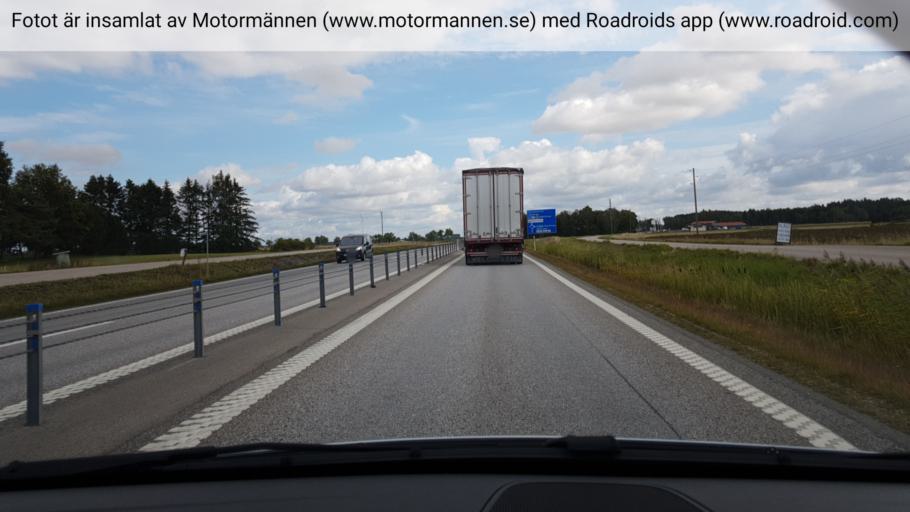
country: SE
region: Vaestra Goetaland
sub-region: Grastorps Kommun
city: Graestorp
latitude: 58.3309
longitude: 12.6013
